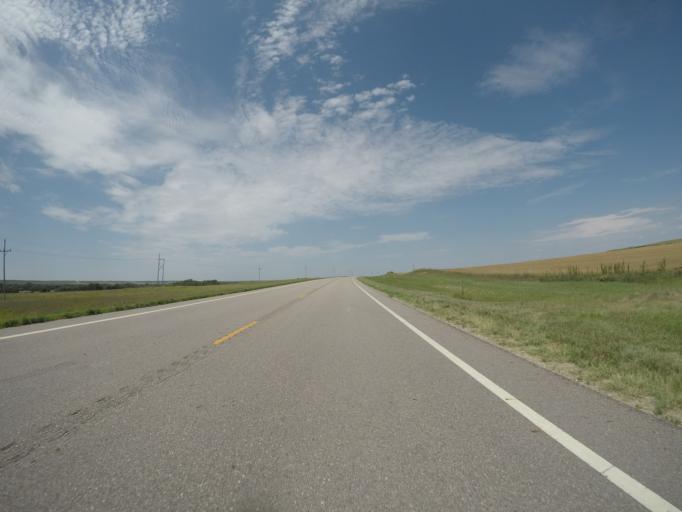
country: US
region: Kansas
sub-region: Rooks County
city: Stockton
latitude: 39.4453
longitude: -99.1583
